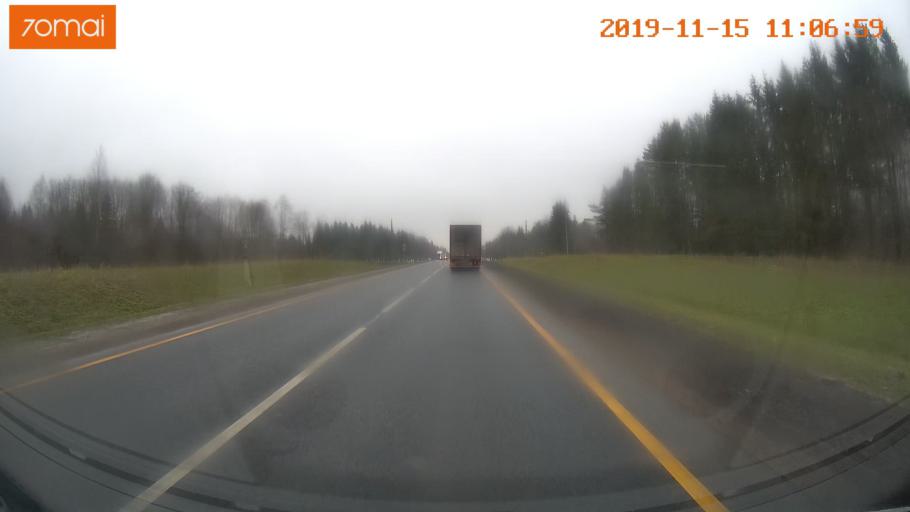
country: RU
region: Vologda
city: Chebsara
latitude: 59.1191
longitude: 39.0416
